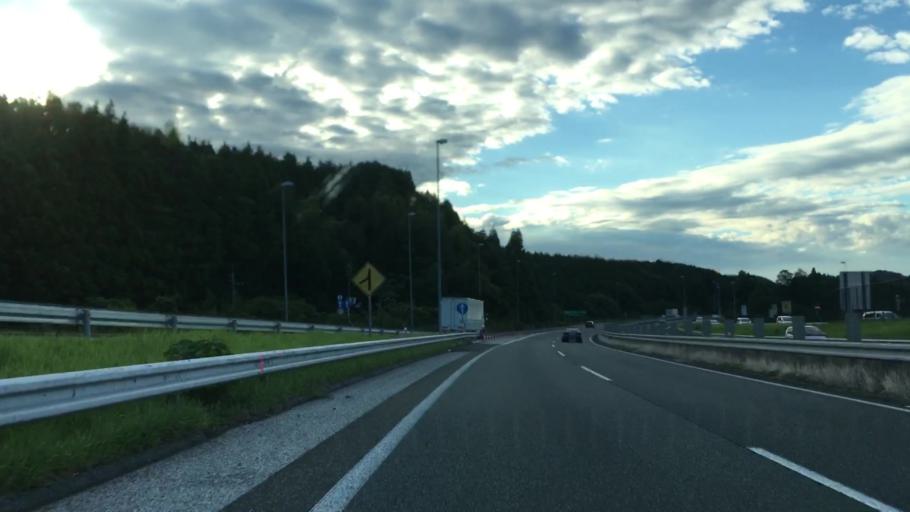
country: JP
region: Yamaguchi
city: Ogori-shimogo
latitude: 34.1541
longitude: 131.3362
